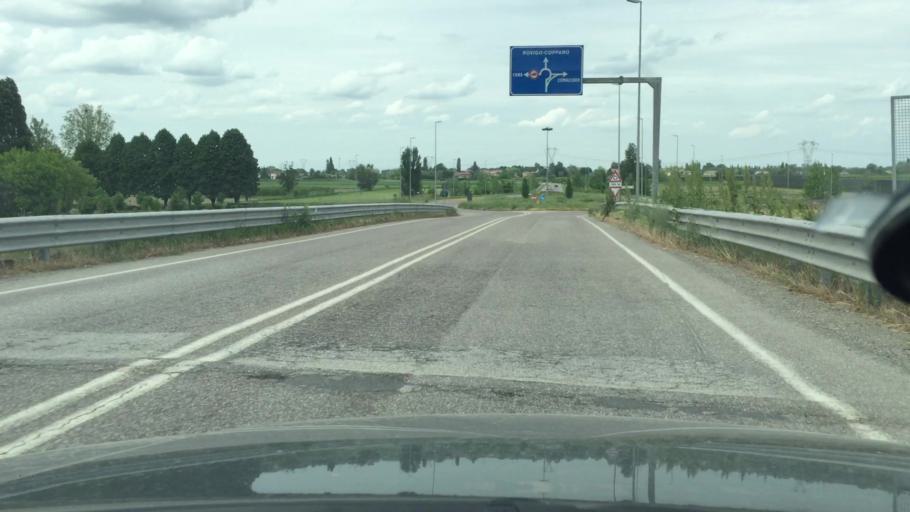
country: IT
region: Emilia-Romagna
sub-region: Provincia di Ferrara
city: Cona
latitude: 44.8030
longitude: 11.7209
